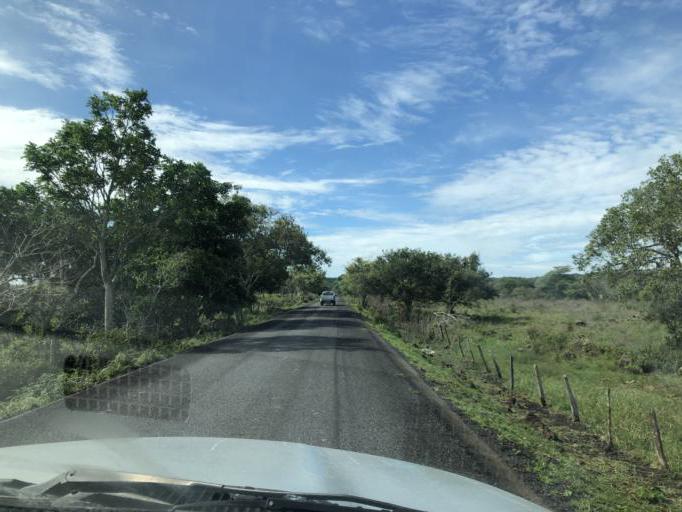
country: MX
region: Veracruz
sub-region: Alto Lucero de Gutierrez Barrios
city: Palma Sola
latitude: 19.7882
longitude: -96.5528
